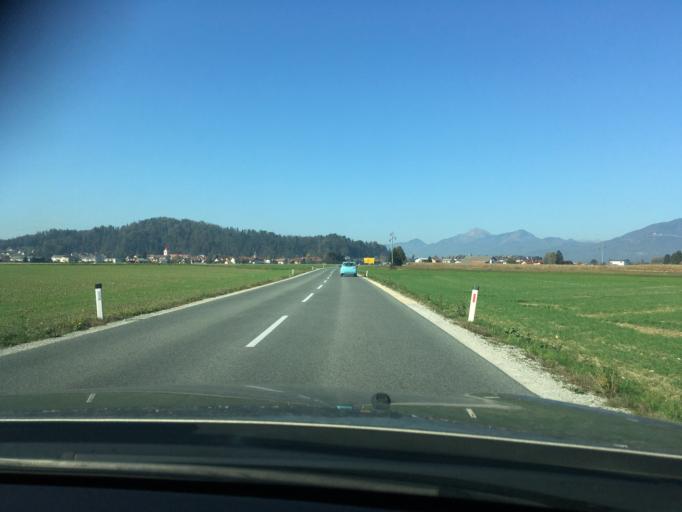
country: SI
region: Menges
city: Menges
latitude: 46.1581
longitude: 14.5833
